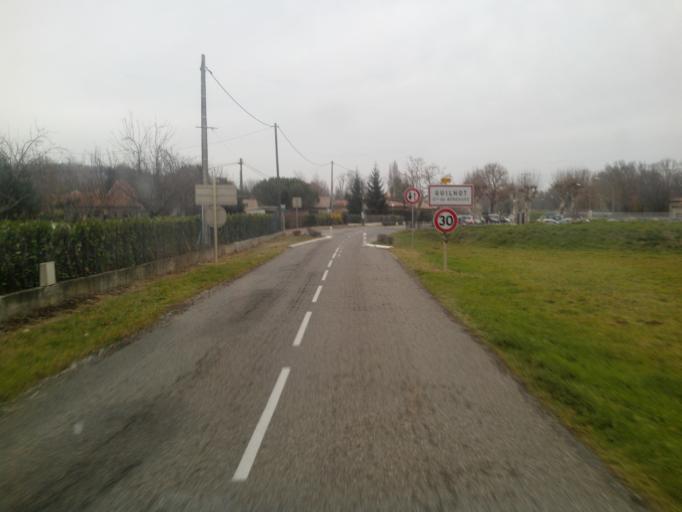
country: FR
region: Midi-Pyrenees
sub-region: Departement de l'Ariege
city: Saint-Jean-du-Falga
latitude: 43.0696
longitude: 1.6176
